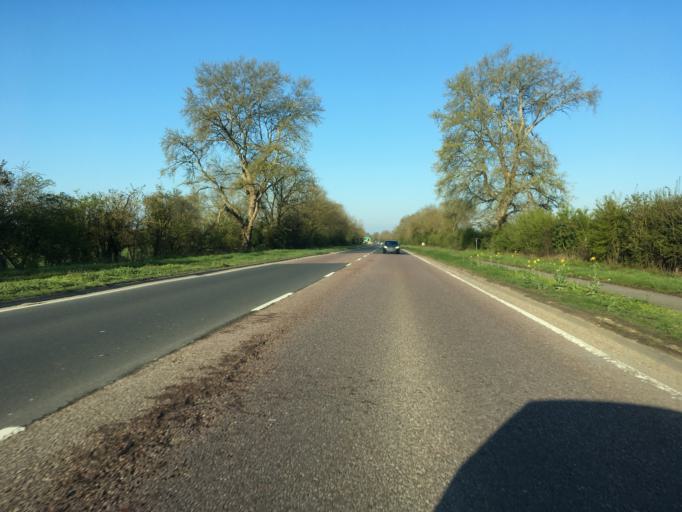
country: GB
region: England
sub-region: Oxfordshire
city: Eynsham
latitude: 51.7892
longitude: -1.3572
